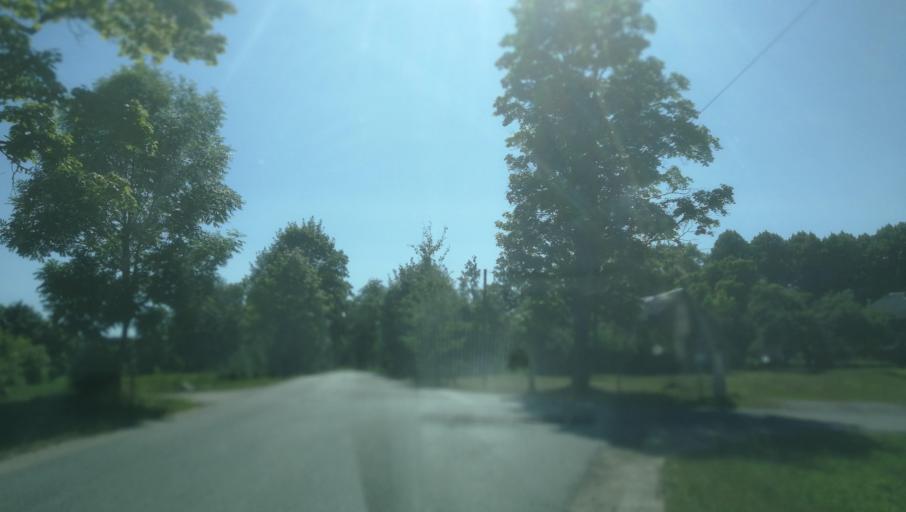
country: LV
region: Cesu Rajons
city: Cesis
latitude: 57.2961
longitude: 25.2356
